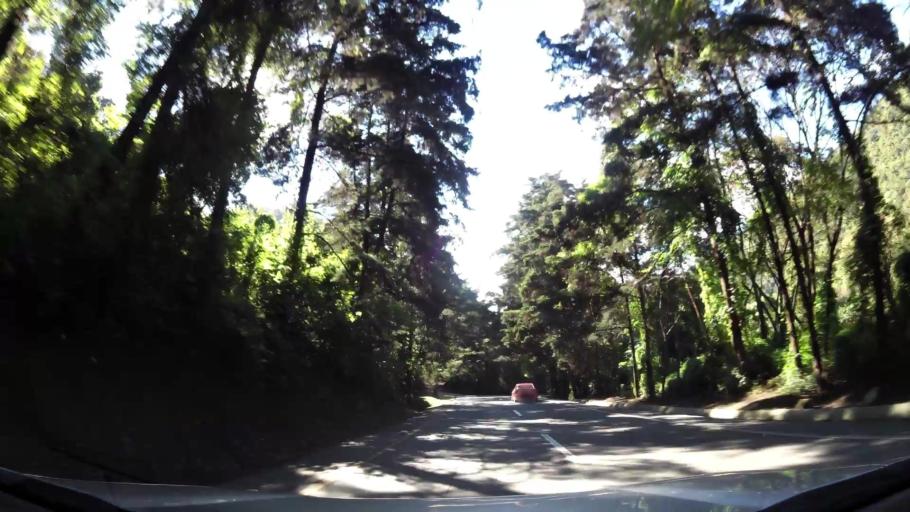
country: GT
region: Sacatepequez
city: Antigua Guatemala
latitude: 14.5594
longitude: -90.7067
